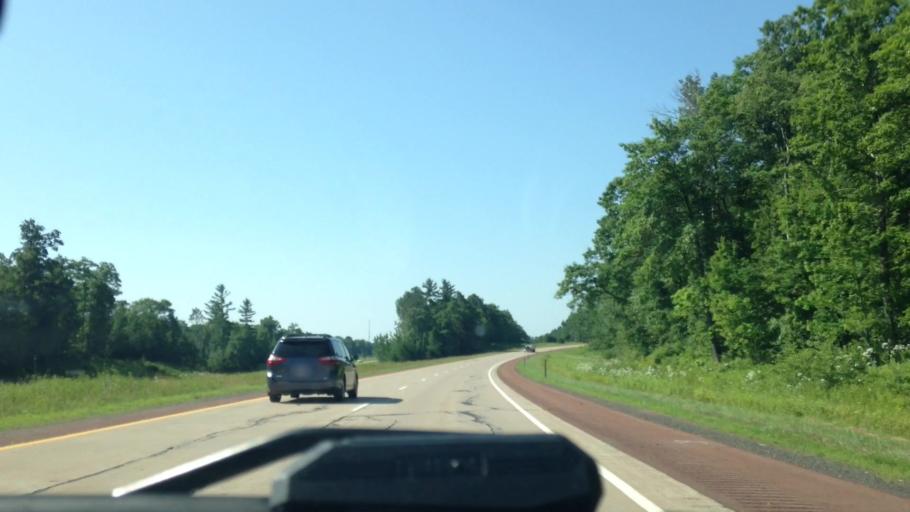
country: US
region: Wisconsin
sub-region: Douglas County
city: Lake Nebagamon
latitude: 46.3923
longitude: -91.8190
